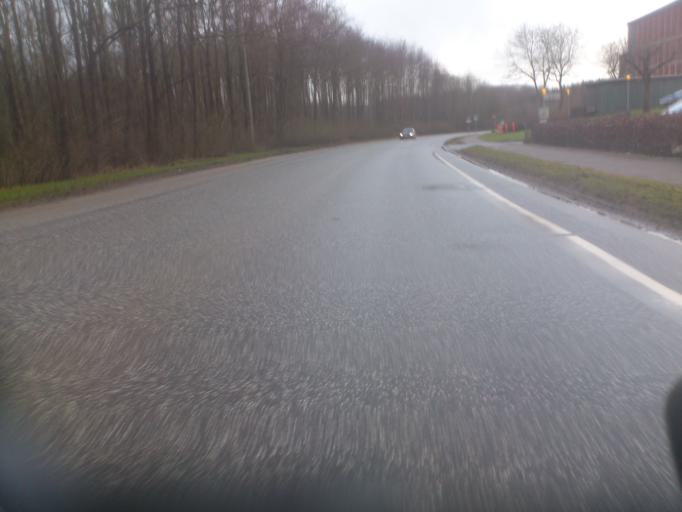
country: DK
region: South Denmark
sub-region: Fredericia Kommune
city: Snoghoj
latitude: 55.5580
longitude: 9.7141
